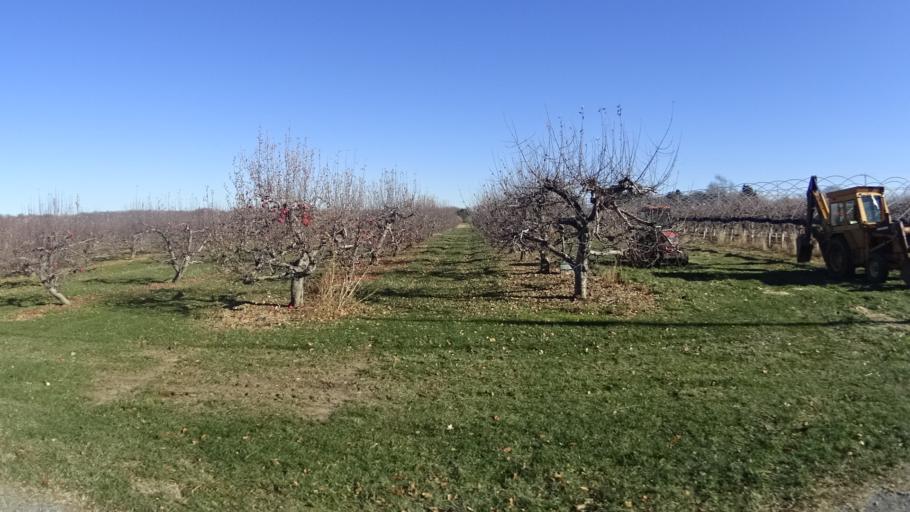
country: US
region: Ohio
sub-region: Lorain County
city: South Amherst
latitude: 41.3671
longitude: -82.3047
